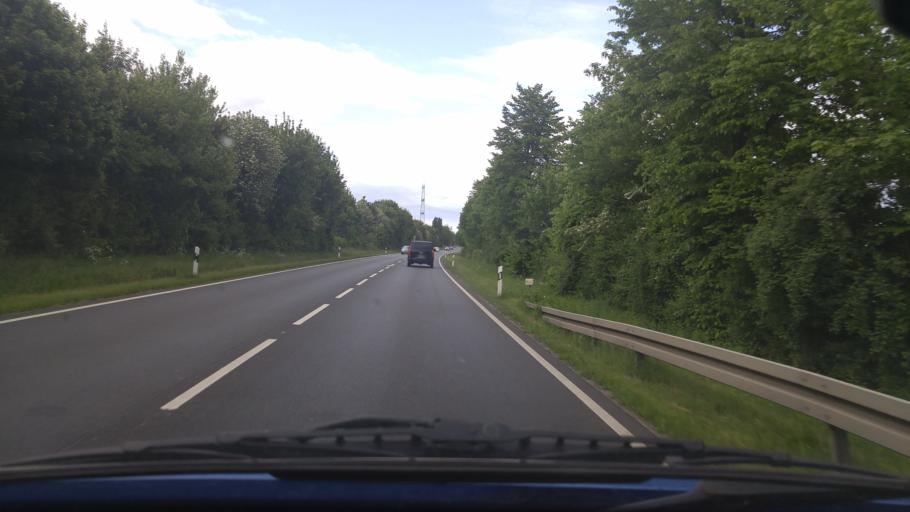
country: DE
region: Hesse
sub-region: Regierungsbezirk Darmstadt
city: Bad Vilbel
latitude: 50.2126
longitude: 8.7353
